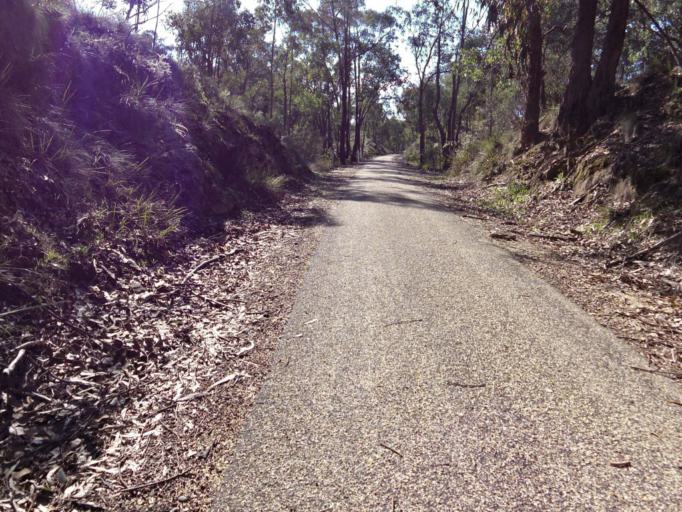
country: AU
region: Victoria
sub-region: Wangaratta
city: Wangaratta
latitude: -36.4065
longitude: 146.6198
